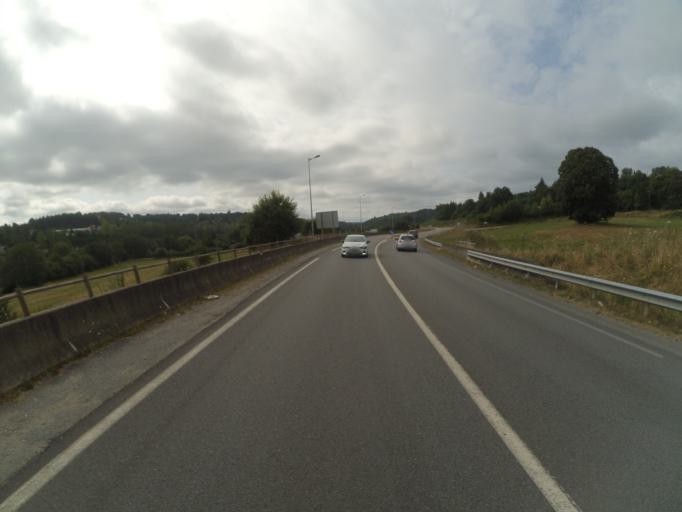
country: FR
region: Limousin
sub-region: Departement de la Correze
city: Ussel
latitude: 45.5391
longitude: 2.3001
